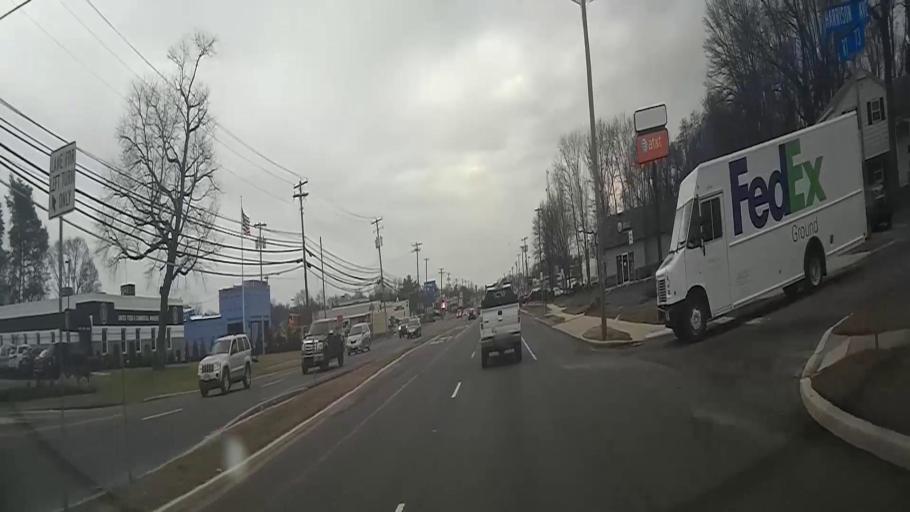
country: US
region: New Jersey
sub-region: Camden County
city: Berlin
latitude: 39.8108
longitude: -74.9308
